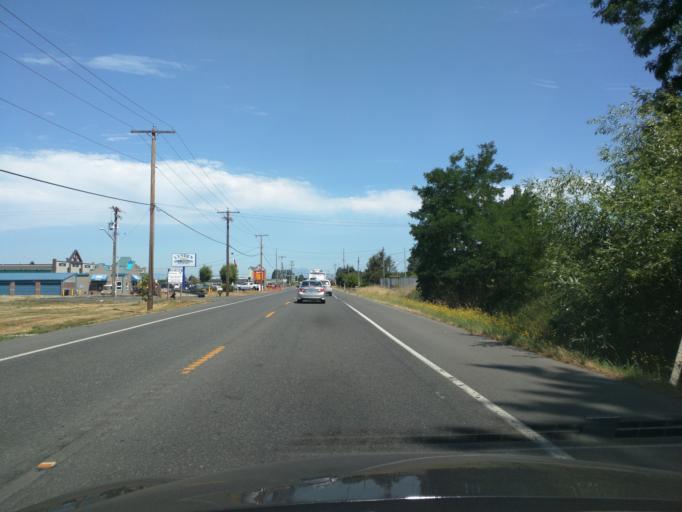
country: US
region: Washington
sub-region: Whatcom County
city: Lynden
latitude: 48.9431
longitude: -122.4854
